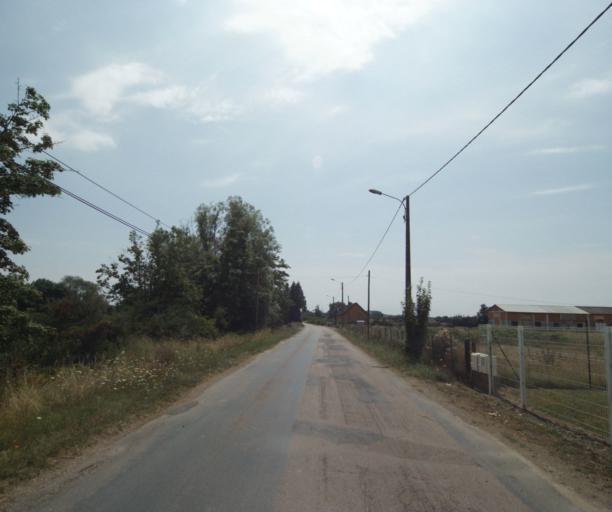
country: FR
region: Bourgogne
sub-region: Departement de Saone-et-Loire
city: Gueugnon
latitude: 46.5934
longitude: 4.0523
